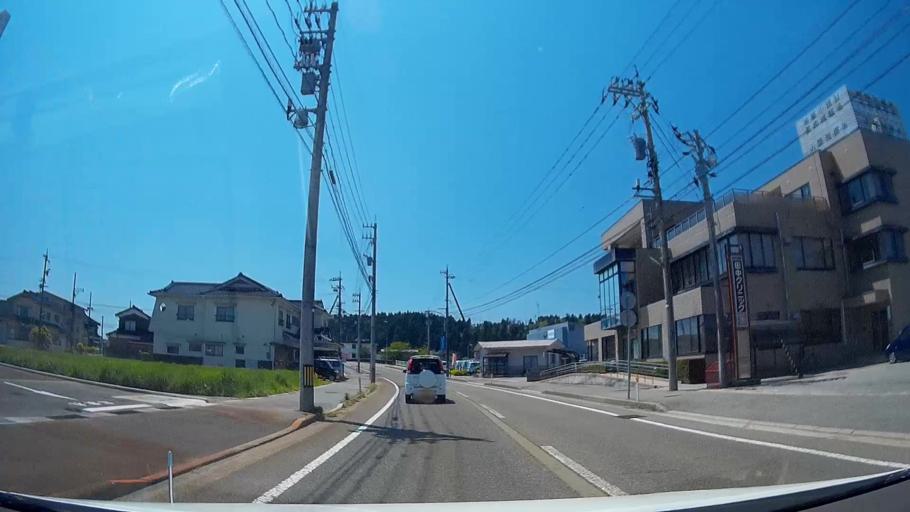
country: JP
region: Ishikawa
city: Nanao
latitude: 37.4408
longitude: 137.2685
